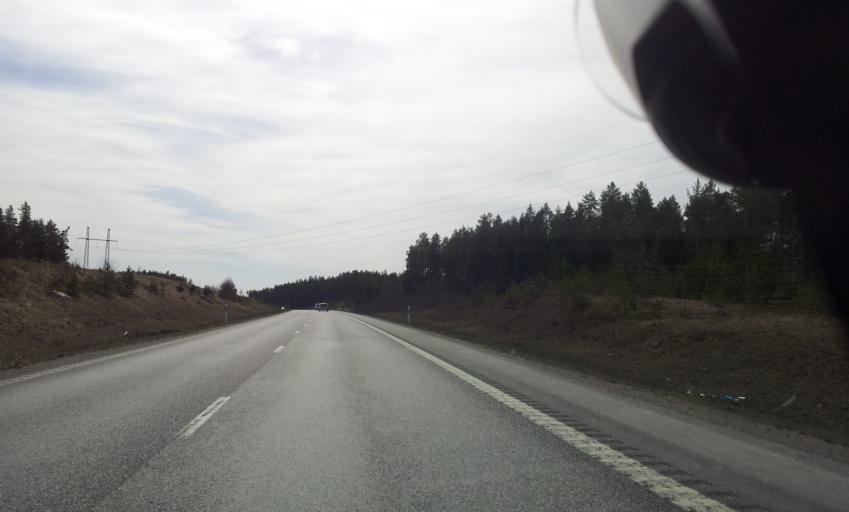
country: SE
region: Uppsala
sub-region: Tierps Kommun
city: Tierp
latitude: 60.2890
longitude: 17.5075
